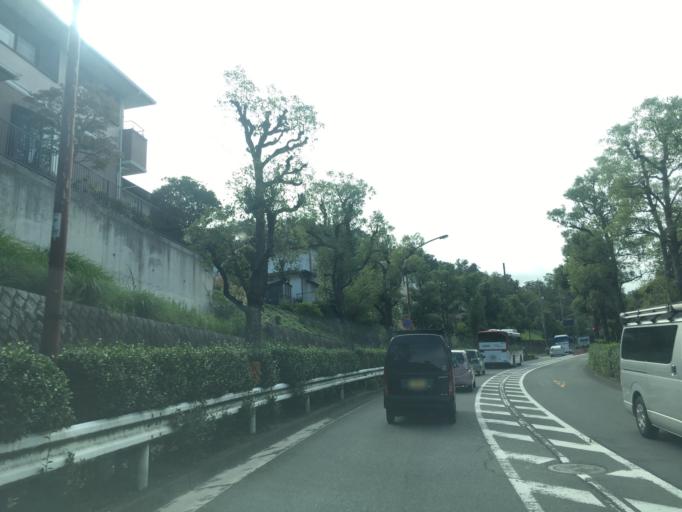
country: JP
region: Tokyo
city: Hino
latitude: 35.6432
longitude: 139.3878
